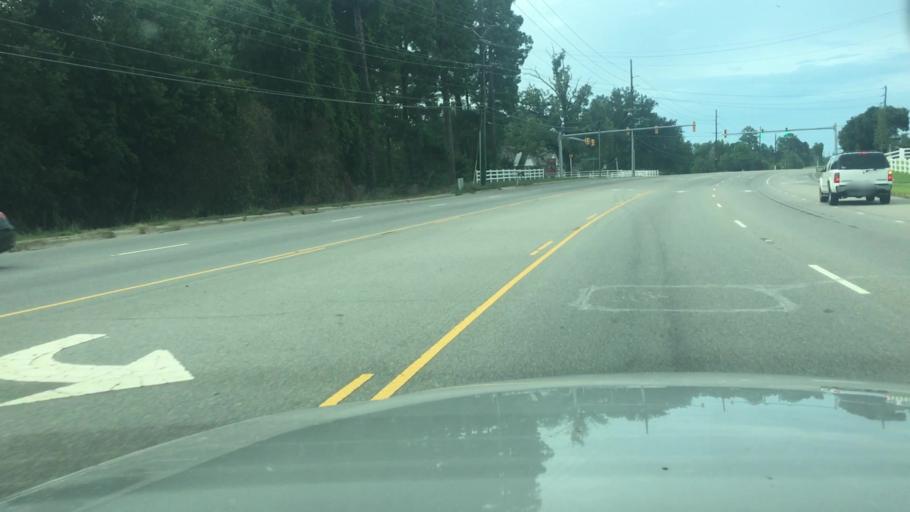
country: US
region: North Carolina
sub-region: Cumberland County
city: Eastover
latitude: 35.1587
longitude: -78.8689
